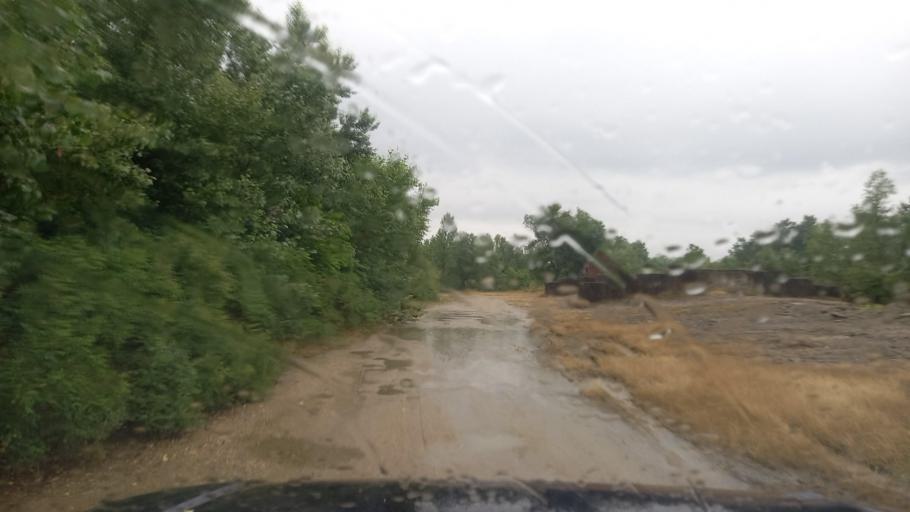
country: RU
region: Krasnodarskiy
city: Vasyurinskaya
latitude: 45.0339
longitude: 39.4710
